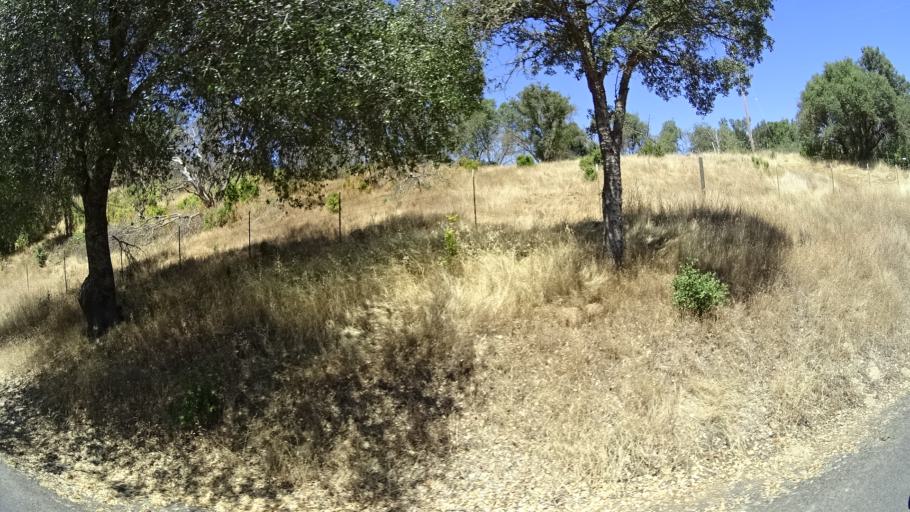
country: US
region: California
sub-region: Calaveras County
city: Copperopolis
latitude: 37.9708
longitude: -120.6932
